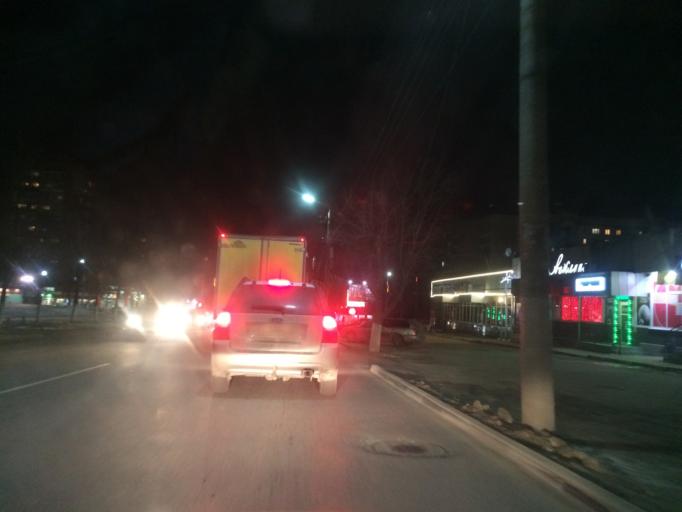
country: RU
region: Tula
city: Tula
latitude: 54.2012
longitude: 37.6498
